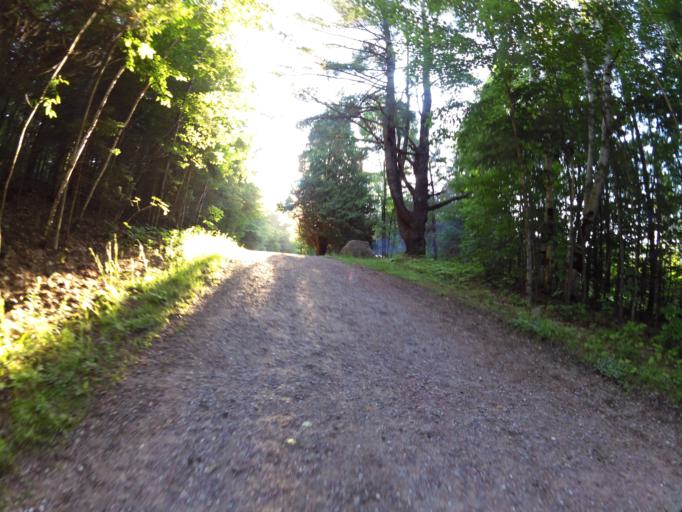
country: CA
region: Quebec
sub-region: Outaouais
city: Wakefield
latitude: 45.5988
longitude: -75.9967
